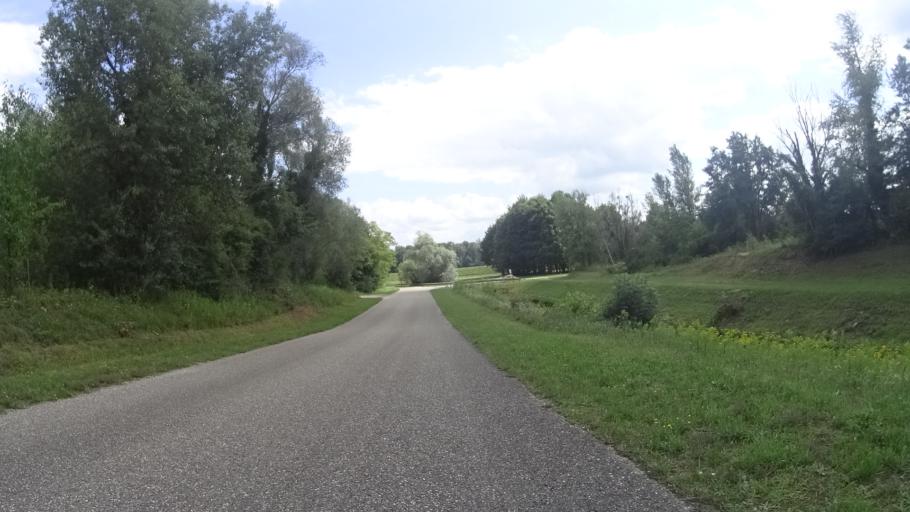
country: DE
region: Baden-Wuerttemberg
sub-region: Karlsruhe Region
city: Greffern
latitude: 48.7639
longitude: 7.9875
